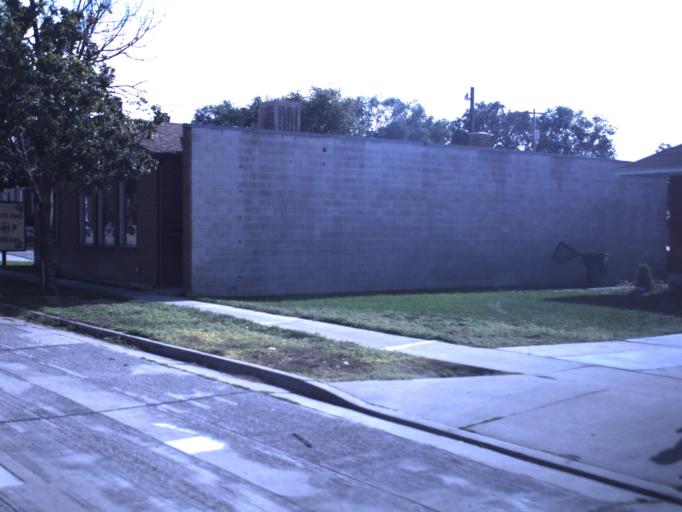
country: US
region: Utah
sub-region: Weber County
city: Harrisville
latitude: 41.2551
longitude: -111.9699
